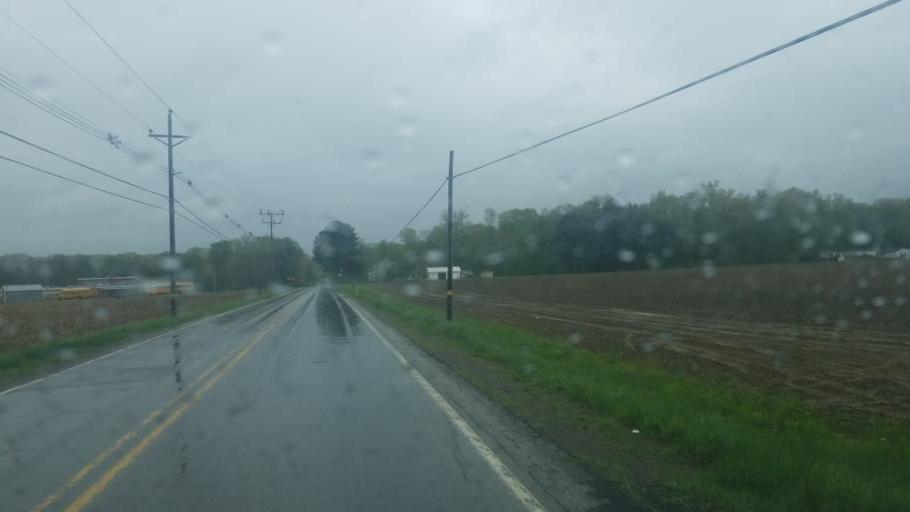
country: US
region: Pennsylvania
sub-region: Forest County
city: Tionesta
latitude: 41.3952
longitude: -79.3523
